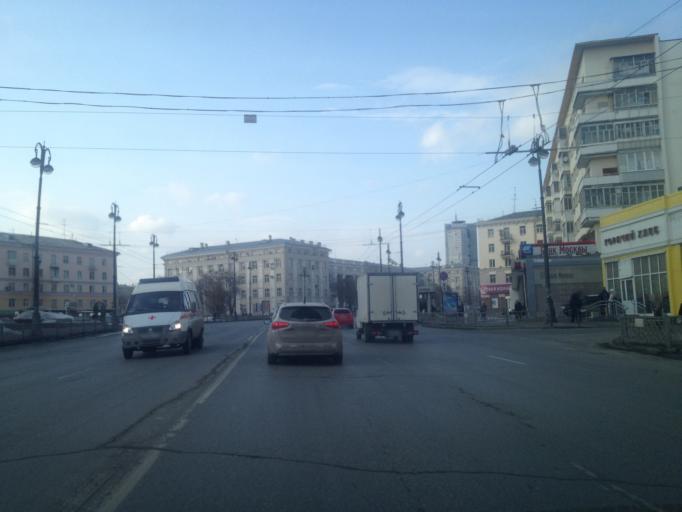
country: RU
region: Sverdlovsk
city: Yekaterinburg
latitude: 56.8491
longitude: 60.6074
